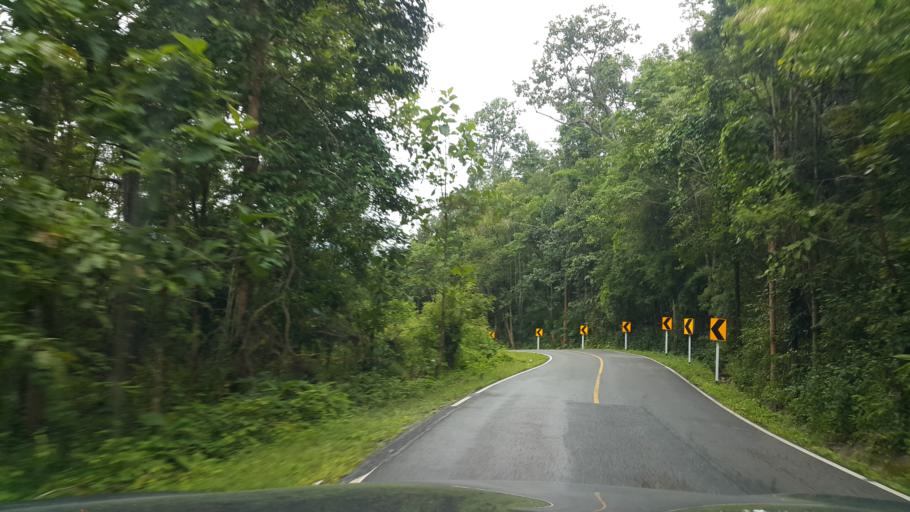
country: TH
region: Chiang Mai
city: Samoeng
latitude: 18.8581
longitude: 98.6594
